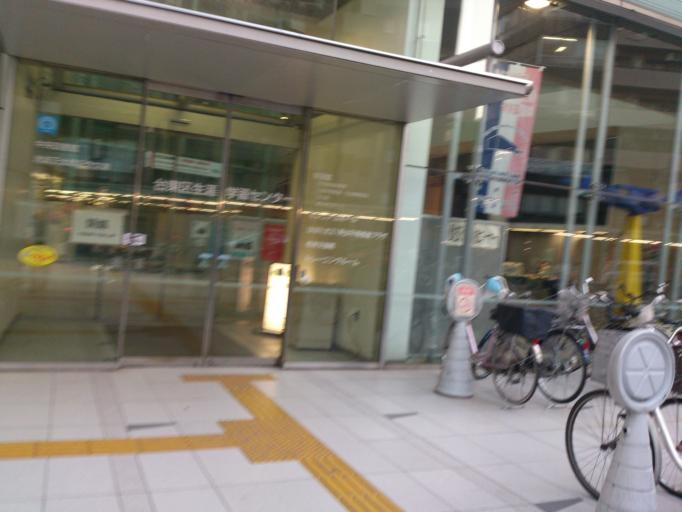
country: JP
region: Tokyo
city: Tokyo
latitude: 35.7175
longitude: 139.7893
